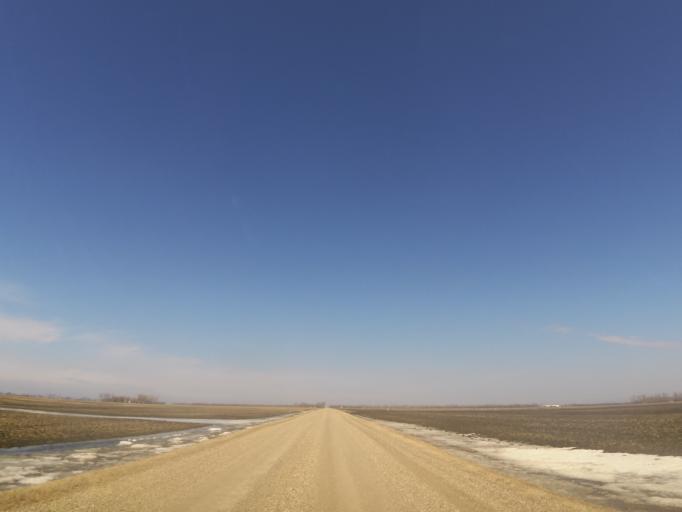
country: US
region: North Dakota
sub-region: Walsh County
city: Grafton
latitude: 48.4170
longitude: -97.2121
